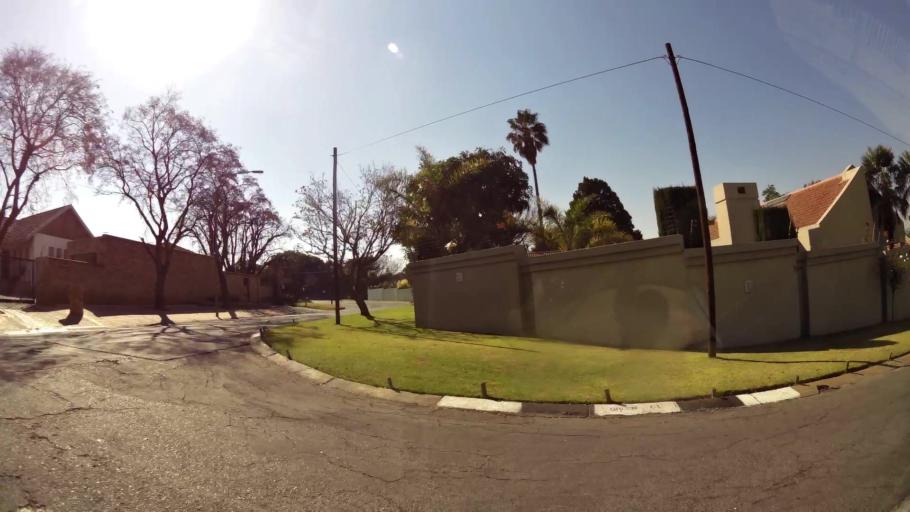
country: ZA
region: Gauteng
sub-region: City of Johannesburg Metropolitan Municipality
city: Johannesburg
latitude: -26.1449
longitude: 28.1018
